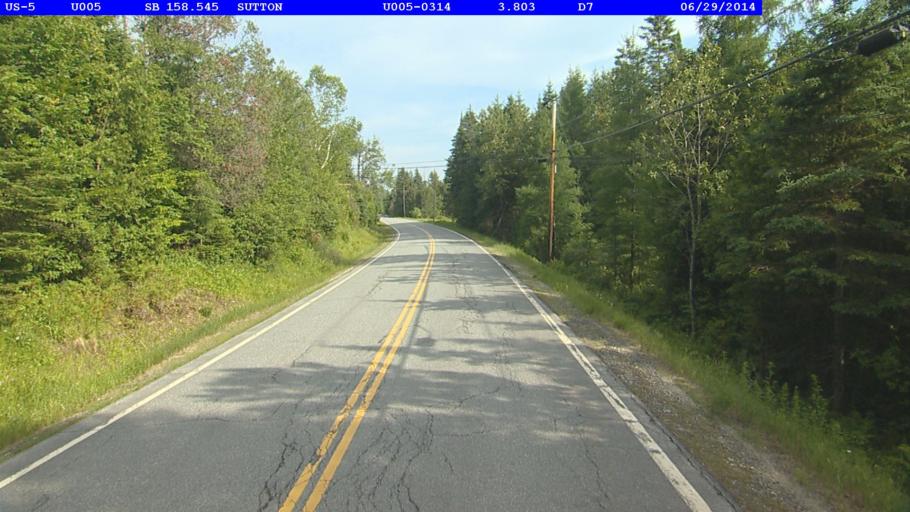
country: US
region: Vermont
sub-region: Caledonia County
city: Lyndonville
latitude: 44.6800
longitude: -72.0338
